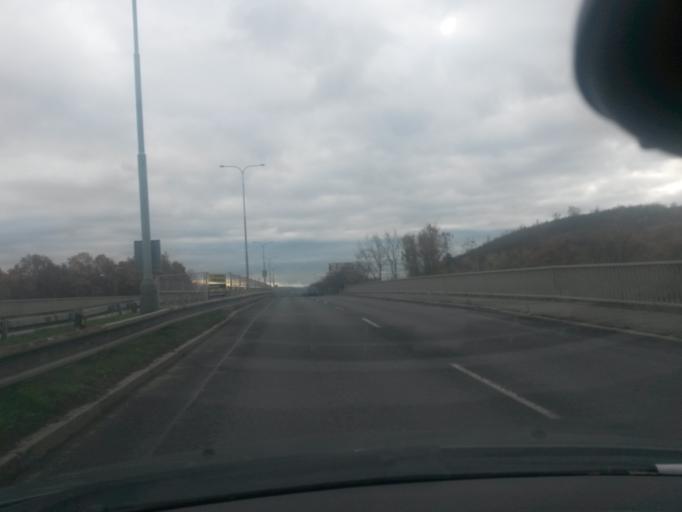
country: CZ
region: Central Bohemia
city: Vestec
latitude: 50.0231
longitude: 14.5087
